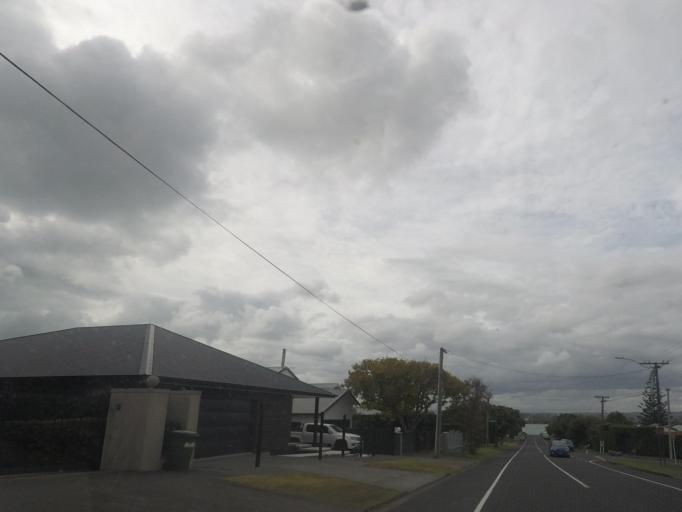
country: NZ
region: Auckland
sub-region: Auckland
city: Tamaki
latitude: -36.8700
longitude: 174.8789
